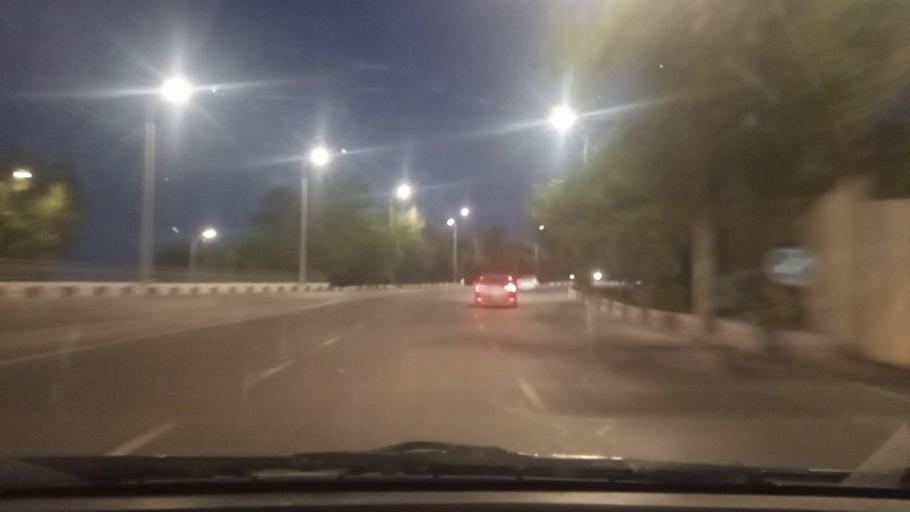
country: UZ
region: Toshkent Shahri
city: Tashkent
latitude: 41.2610
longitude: 69.2288
